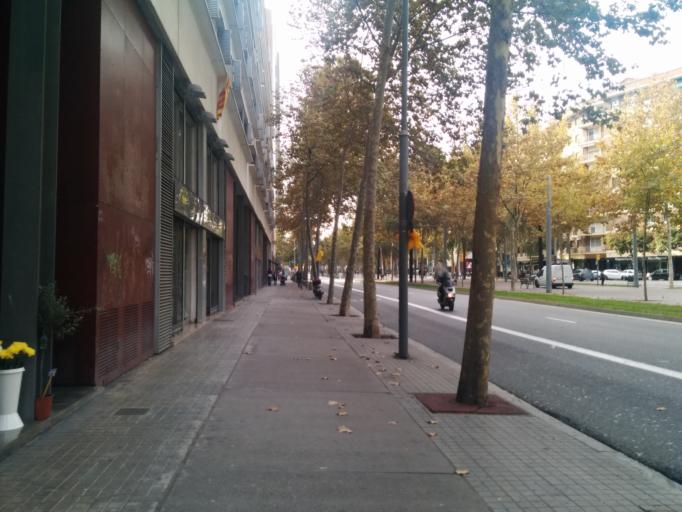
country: ES
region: Catalonia
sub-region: Provincia de Barcelona
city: Sant Marti
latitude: 41.4053
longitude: 2.1955
